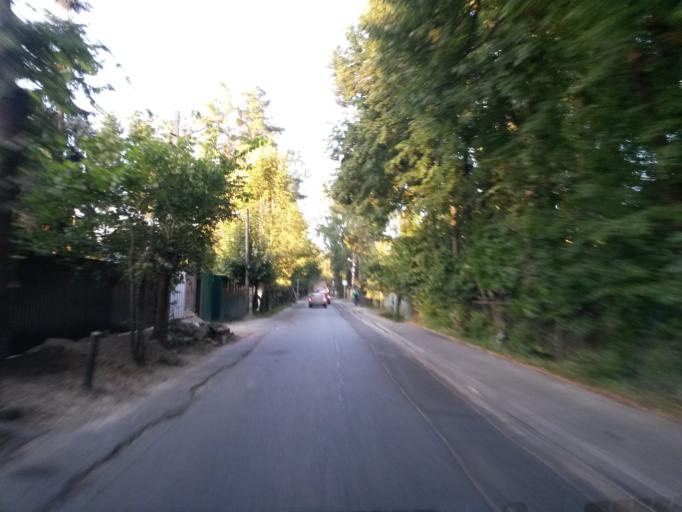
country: RU
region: Moskovskaya
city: Mamontovka
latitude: 55.9816
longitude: 37.8436
